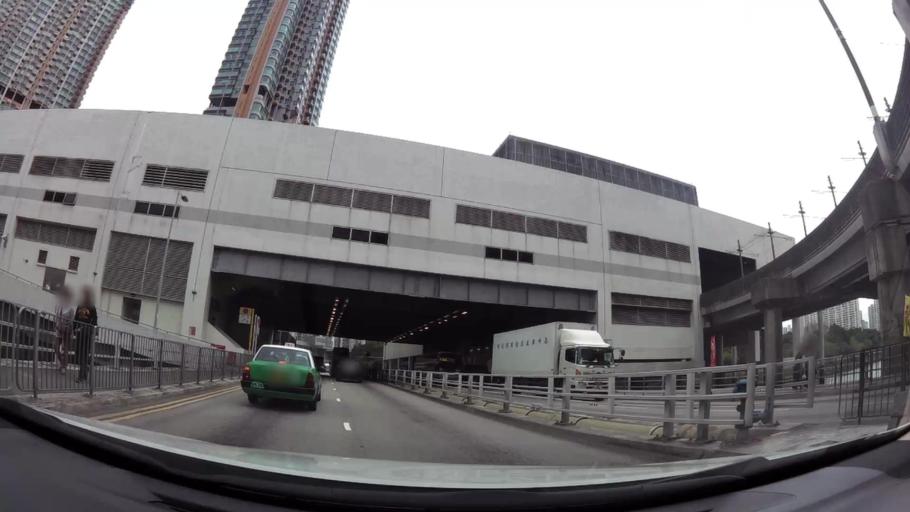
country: HK
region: Tuen Mun
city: Tuen Mun
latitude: 22.3944
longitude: 113.9724
